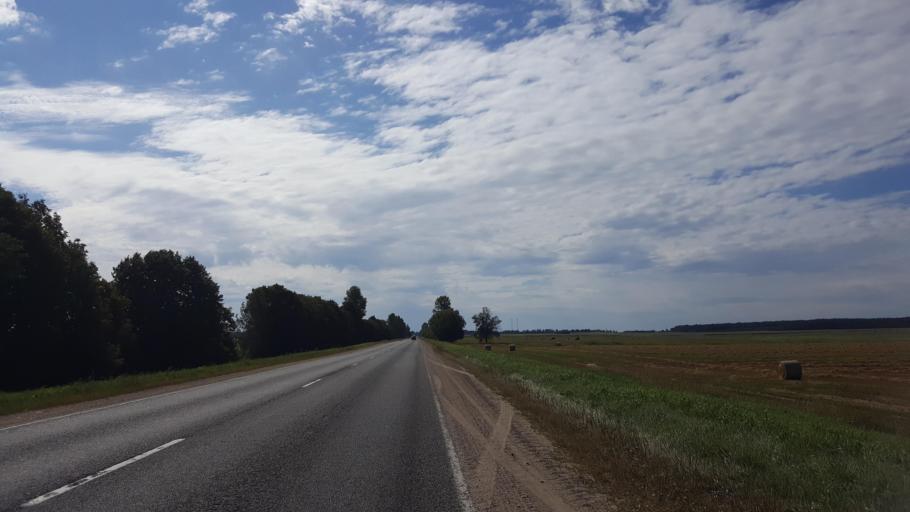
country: BY
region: Brest
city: Kamyanyets
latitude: 52.3649
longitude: 23.8883
